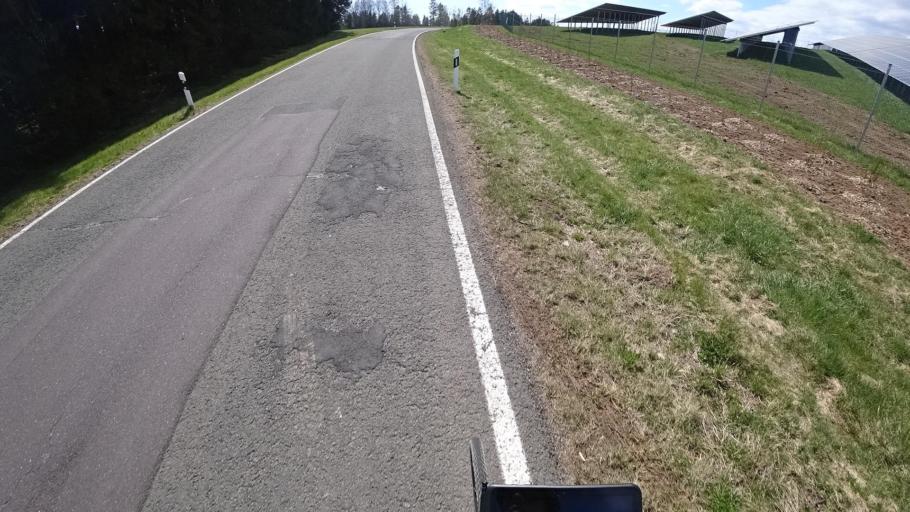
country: DE
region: Rheinland-Pfalz
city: Kell
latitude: 49.6340
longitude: 6.8456
